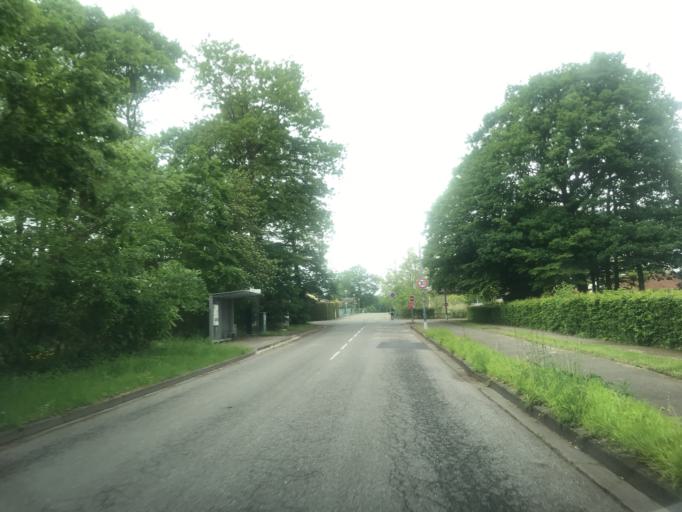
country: FR
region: Haute-Normandie
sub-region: Departement de l'Eure
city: Evreux
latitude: 49.0099
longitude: 1.1383
